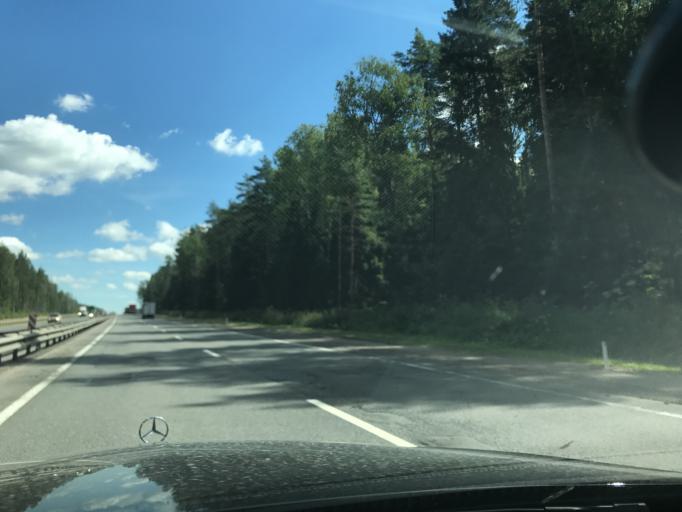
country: RU
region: Vladimir
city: Melekhovo
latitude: 56.2058
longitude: 41.1896
